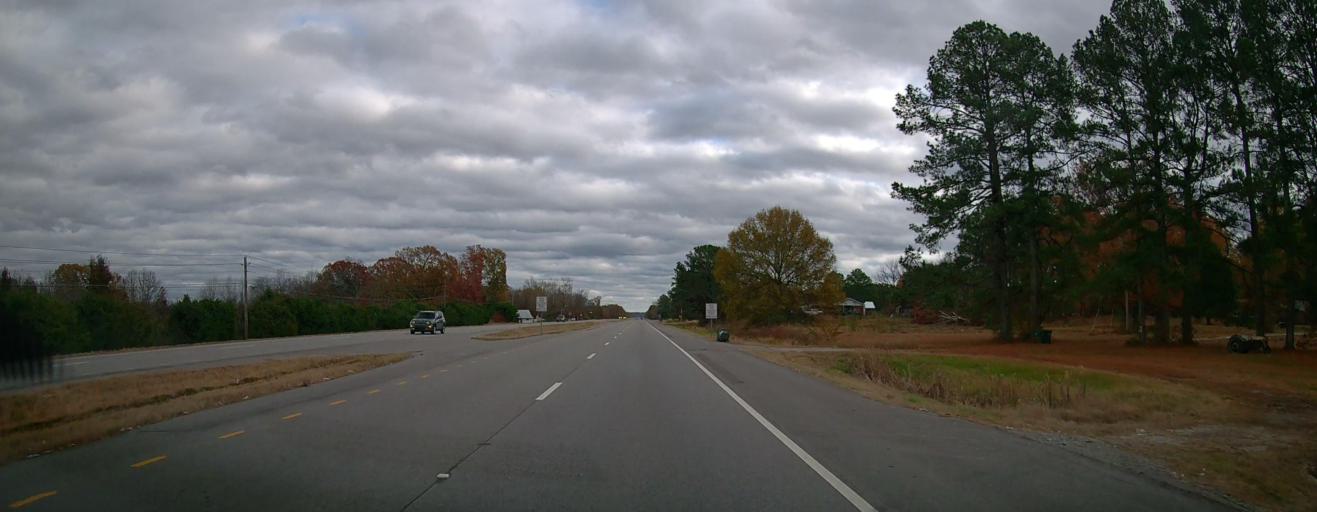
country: US
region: Alabama
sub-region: Colbert County
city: Muscle Shoals
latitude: 34.6642
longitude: -87.5498
